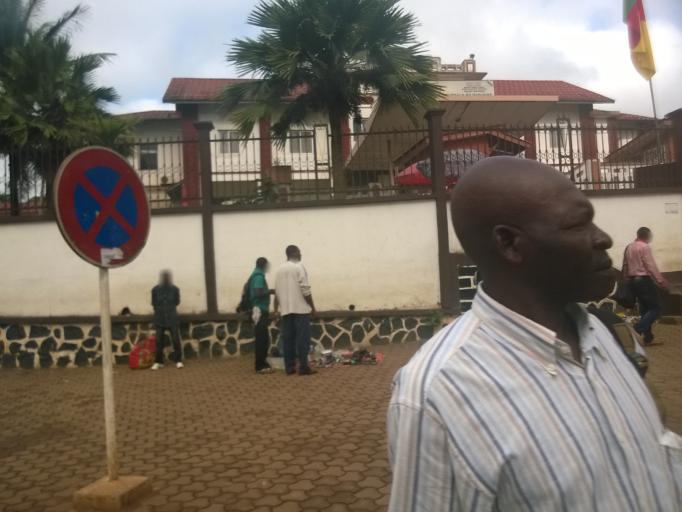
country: CM
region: Centre
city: Yaounde
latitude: 3.8607
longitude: 11.5202
